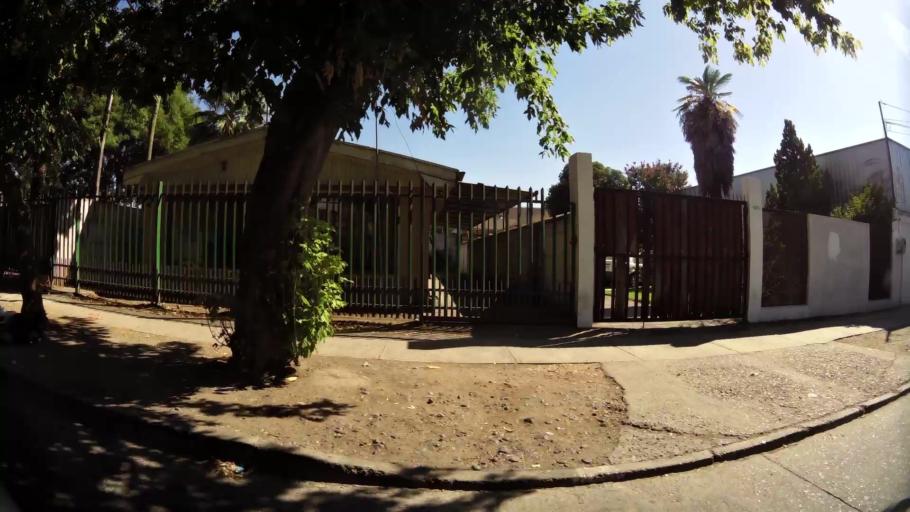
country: CL
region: Maule
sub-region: Provincia de Curico
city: Curico
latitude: -34.9812
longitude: -71.2498
